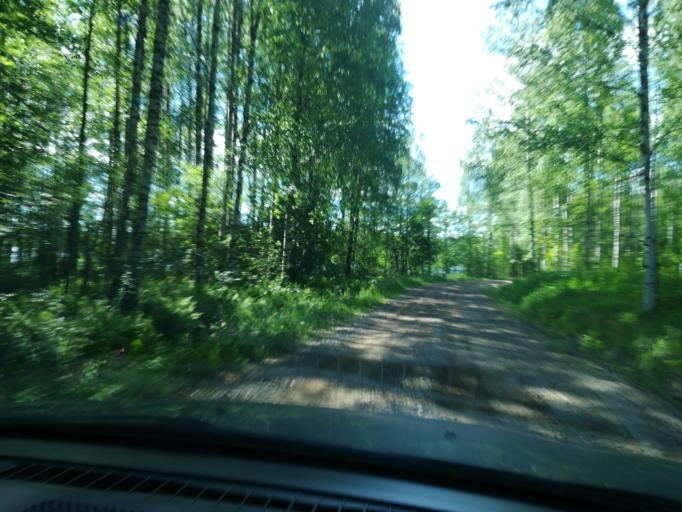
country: FI
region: Southern Savonia
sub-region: Mikkeli
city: Puumala
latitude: 61.6599
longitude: 28.1540
